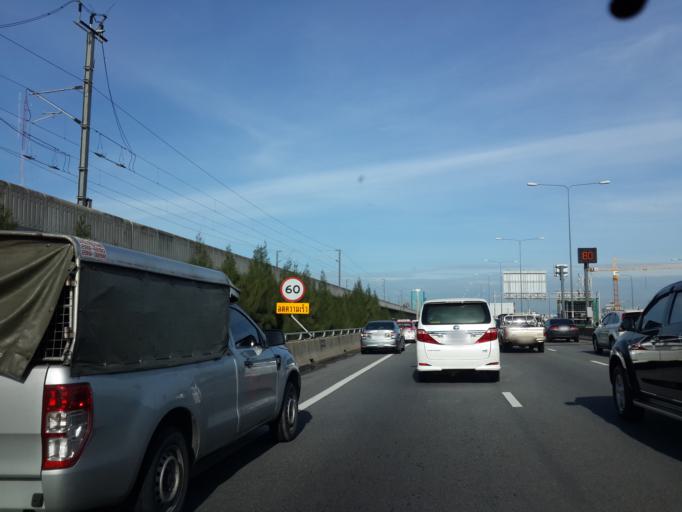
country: TH
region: Bangkok
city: Watthana
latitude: 13.7412
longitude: 100.6182
